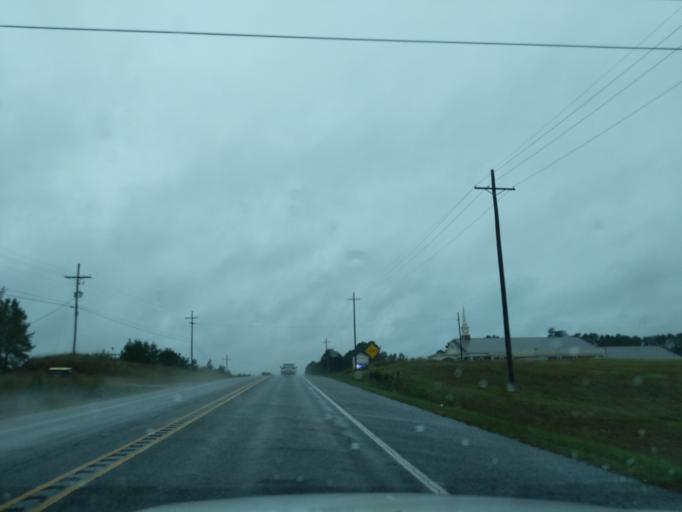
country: US
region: Louisiana
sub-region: Webster Parish
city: Minden
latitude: 32.6110
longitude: -93.2498
